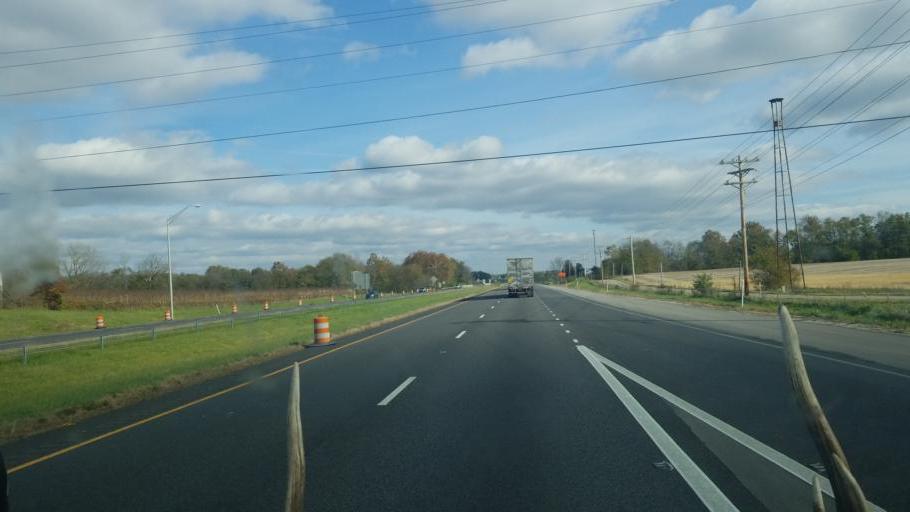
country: US
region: Indiana
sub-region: Wayne County
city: Cambridge City
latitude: 39.8528
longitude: -85.1400
